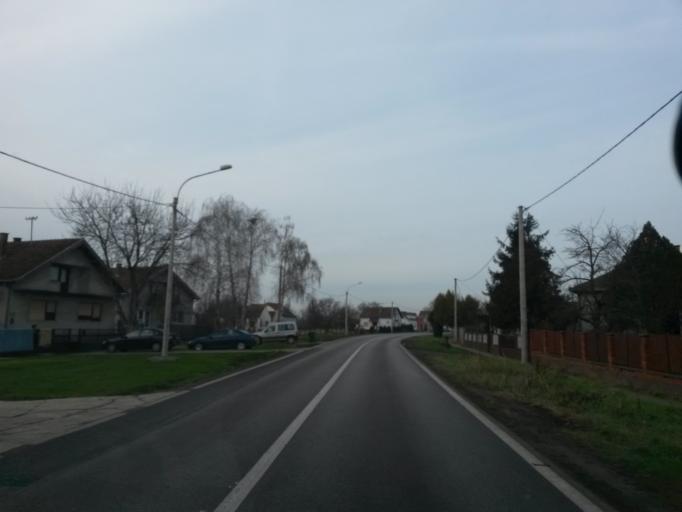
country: HR
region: Vukovarsko-Srijemska
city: Trpinja
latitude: 45.4091
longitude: 18.9064
